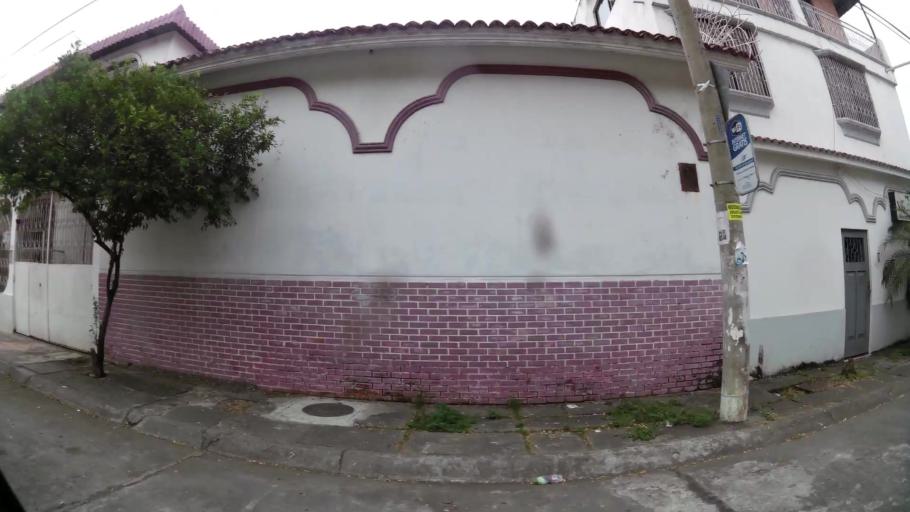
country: EC
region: Guayas
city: Eloy Alfaro
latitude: -2.1320
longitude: -79.8853
